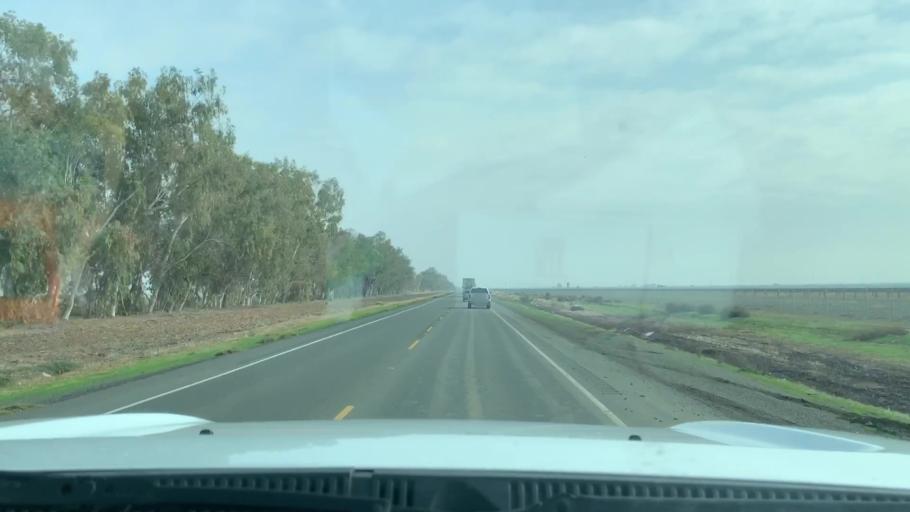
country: US
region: California
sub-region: Kings County
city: Lemoore Station
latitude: 36.2551
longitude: -119.9228
